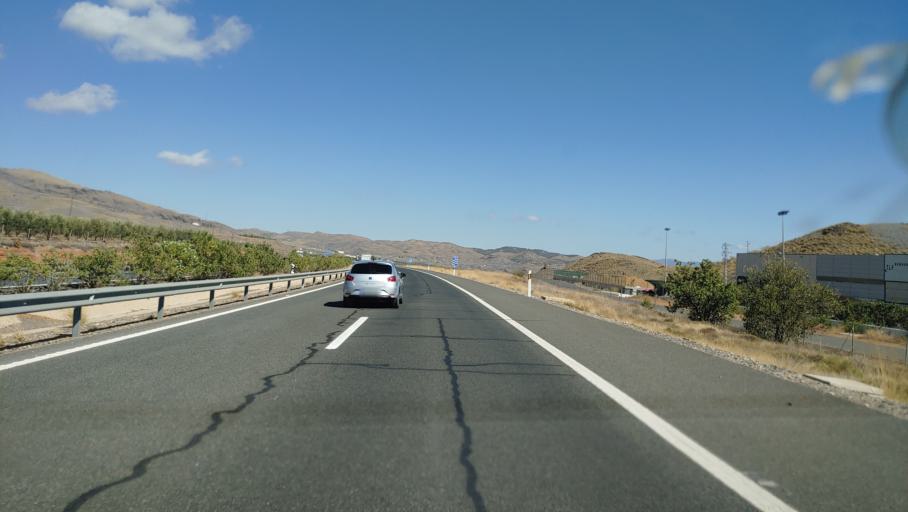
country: ES
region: Andalusia
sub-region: Provincia de Almeria
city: Gergal
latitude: 37.1179
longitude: -2.5735
